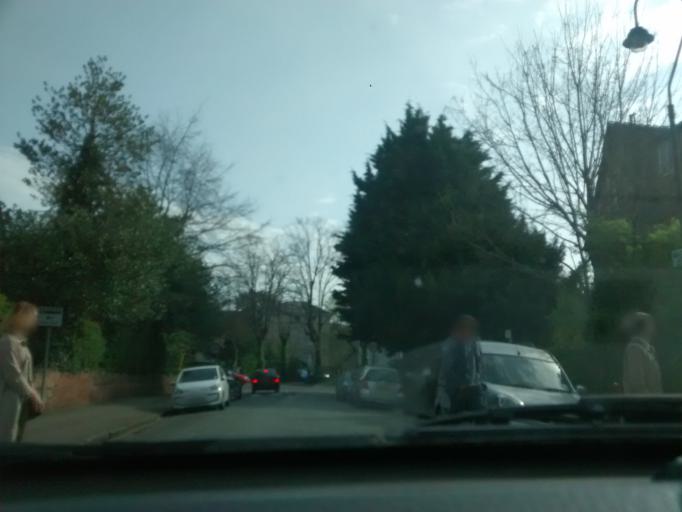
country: GB
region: England
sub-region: Oxfordshire
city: Oxford
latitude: 51.7655
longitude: -1.2618
